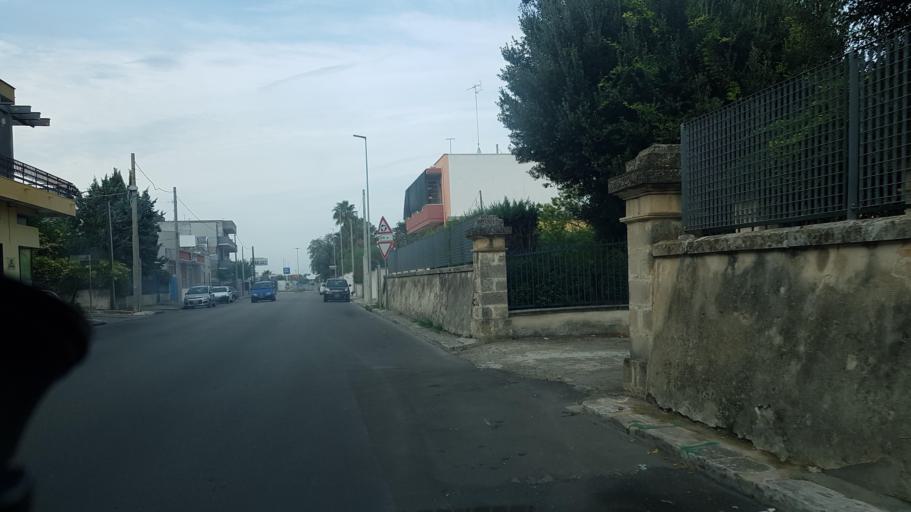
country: IT
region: Apulia
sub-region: Provincia di Lecce
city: Trepuzzi
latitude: 40.4086
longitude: 18.0682
